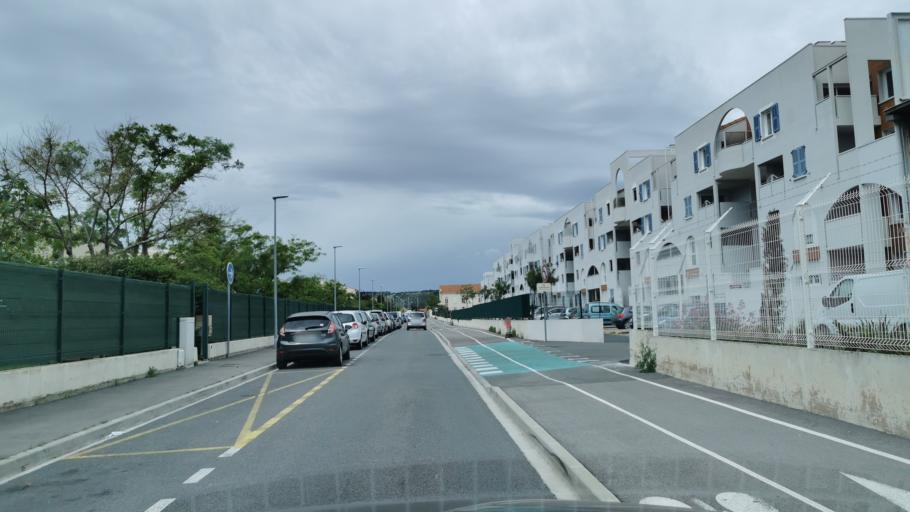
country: FR
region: Languedoc-Roussillon
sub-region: Departement de l'Aude
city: Narbonne
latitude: 43.1775
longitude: 2.9934
